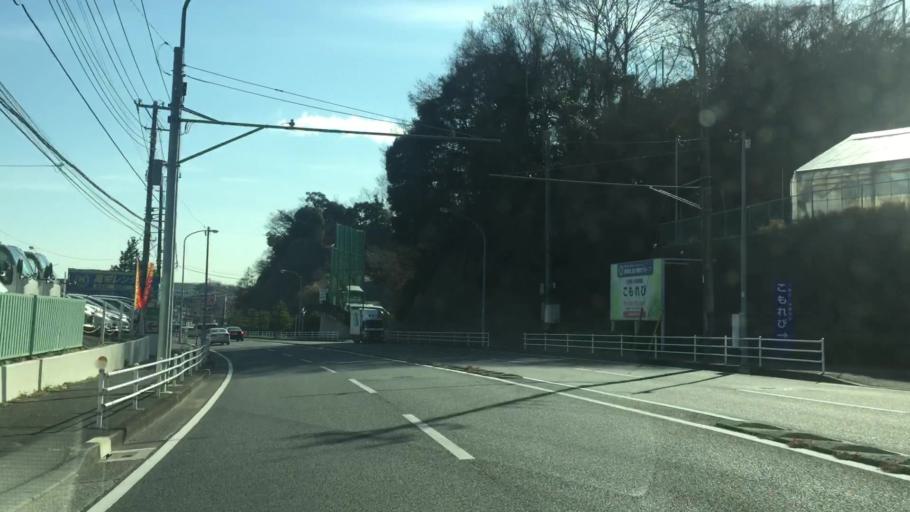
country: JP
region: Kanagawa
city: Zushi
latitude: 35.3509
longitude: 139.6070
